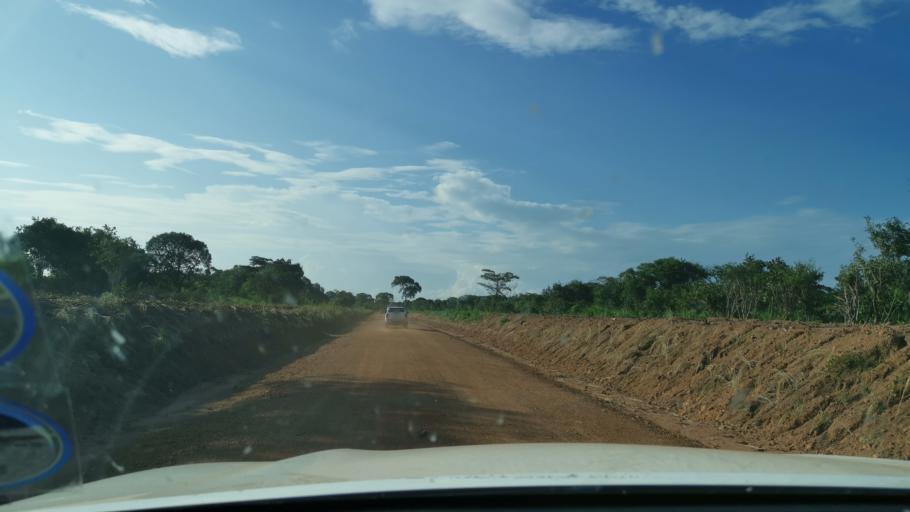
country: ZM
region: Luapula
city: Samfya
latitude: -11.1048
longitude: 29.5735
